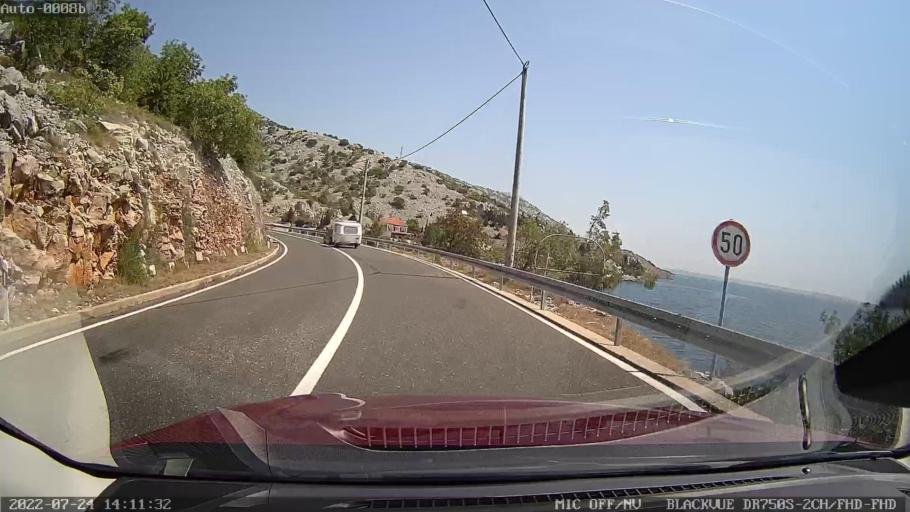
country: HR
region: Zadarska
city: Vrsi
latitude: 44.3905
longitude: 15.2504
